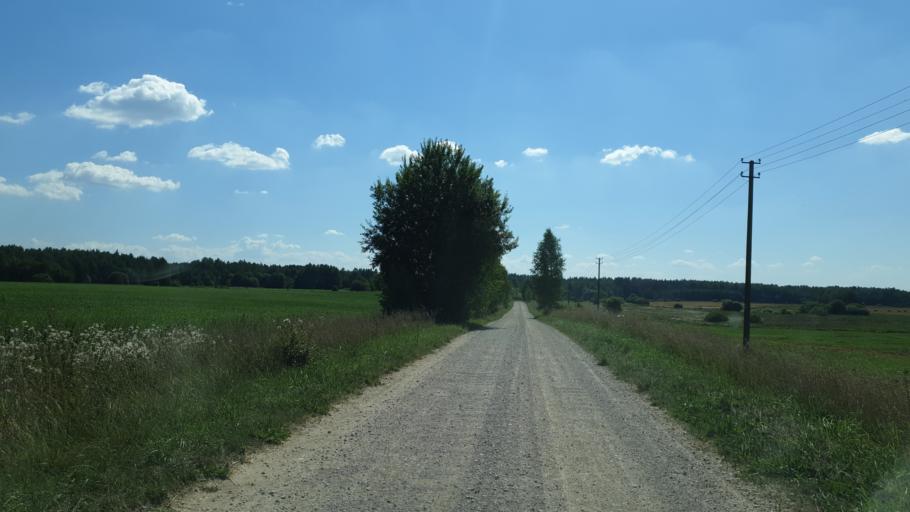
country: LT
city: Sirvintos
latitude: 54.9074
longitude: 24.9112
